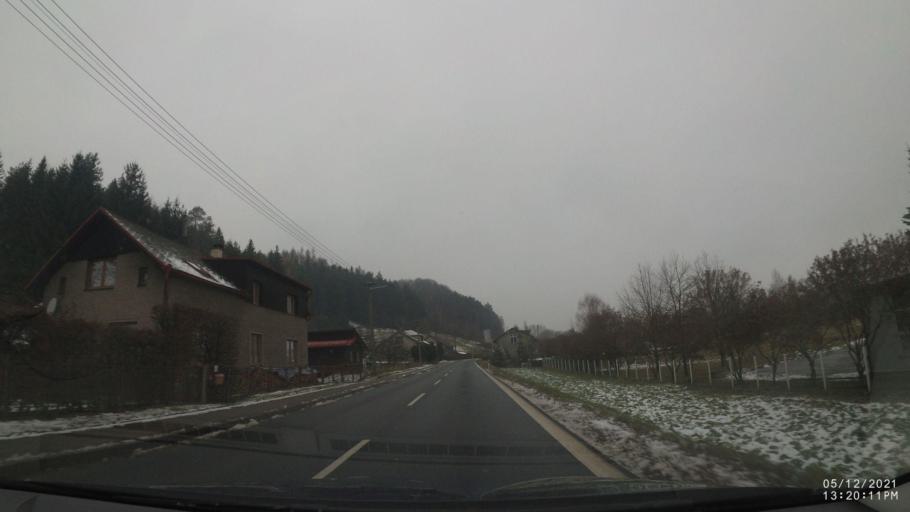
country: CZ
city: Velke Porici
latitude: 50.4479
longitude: 16.1892
